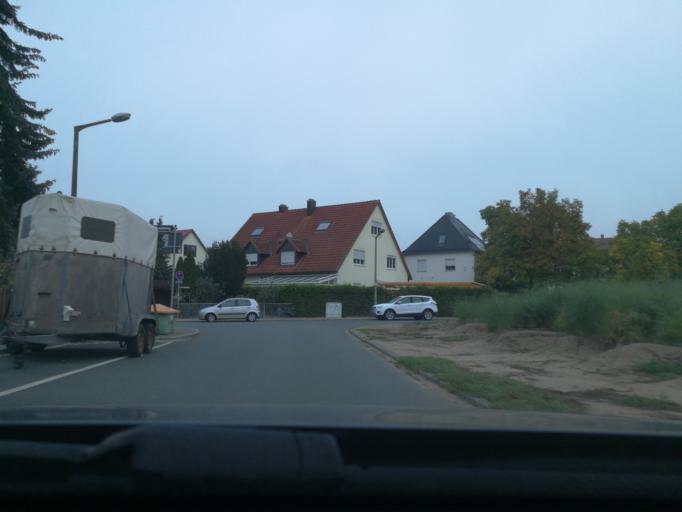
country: DE
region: Bavaria
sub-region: Regierungsbezirk Mittelfranken
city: Furth
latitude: 49.4812
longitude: 11.0114
